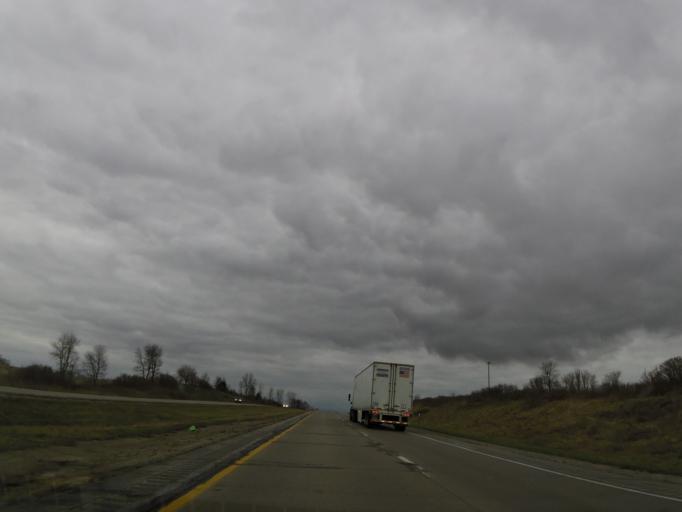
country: US
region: Iowa
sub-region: Johnson County
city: University Heights
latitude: 41.5953
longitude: -91.5470
